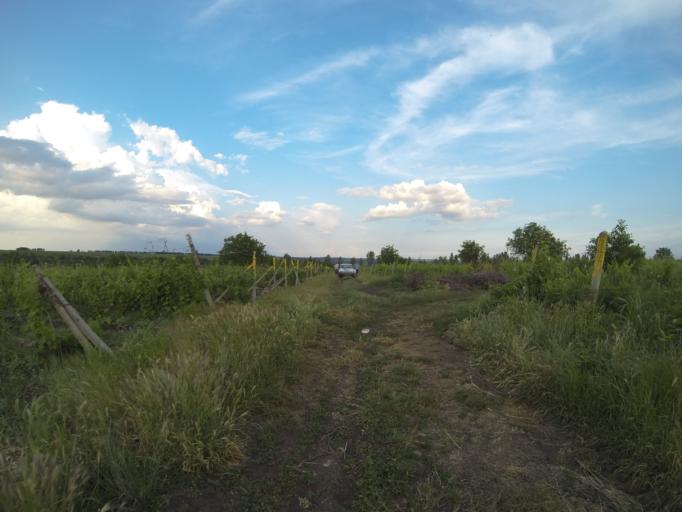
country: RO
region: Dolj
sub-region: Comuna Ceratu
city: Ceratu
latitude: 44.1105
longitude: 23.6863
